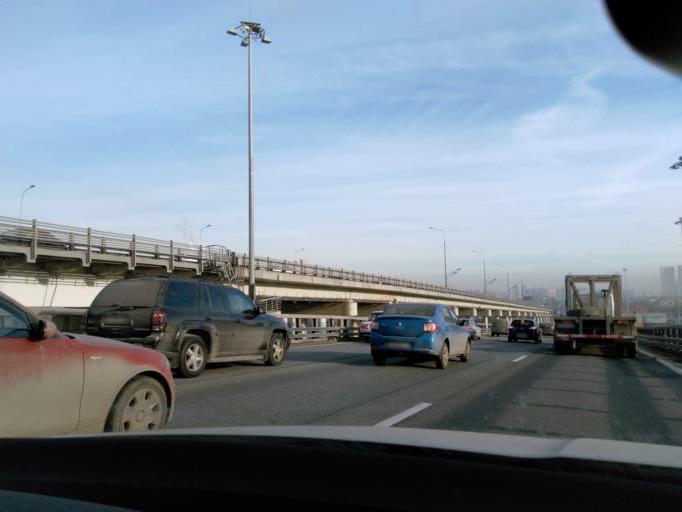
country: RU
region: Moskovskaya
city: Presnenskiy
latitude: 55.7537
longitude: 37.5323
